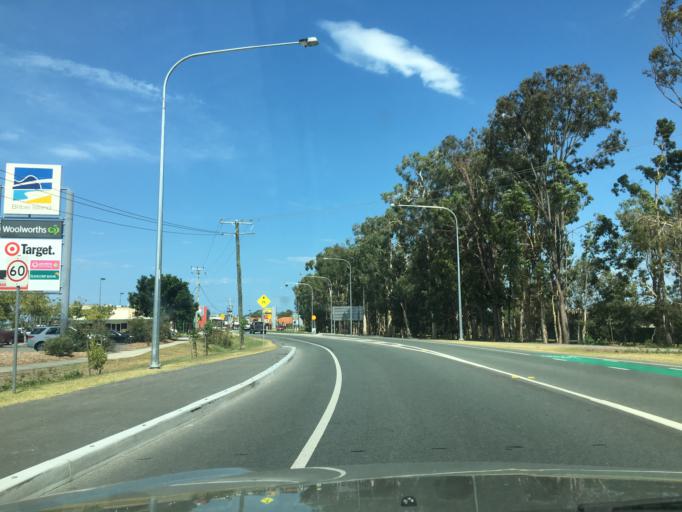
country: AU
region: Queensland
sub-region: Moreton Bay
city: Bongaree
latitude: -27.0644
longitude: 153.1555
